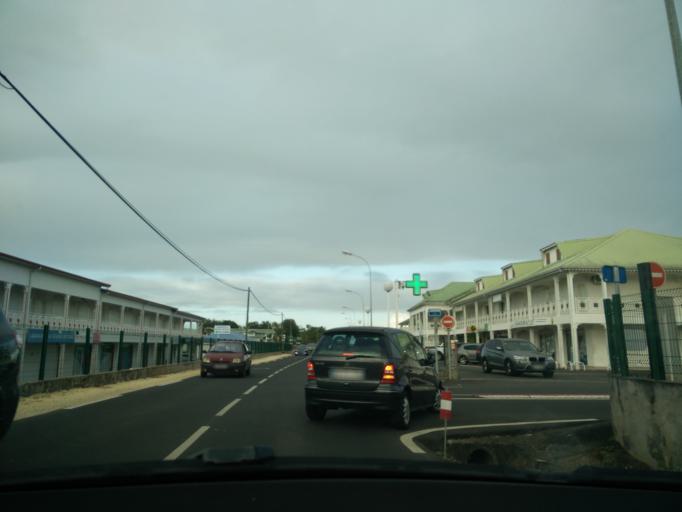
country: GP
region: Guadeloupe
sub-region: Guadeloupe
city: Baie-Mahault
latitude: 16.2412
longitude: -61.5968
